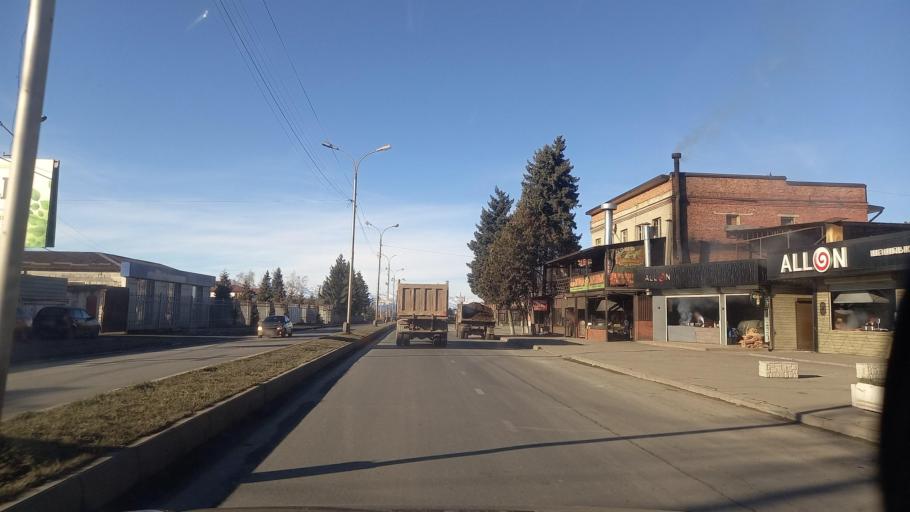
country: RU
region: North Ossetia
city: Vladikavkaz
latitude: 43.0255
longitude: 44.6382
